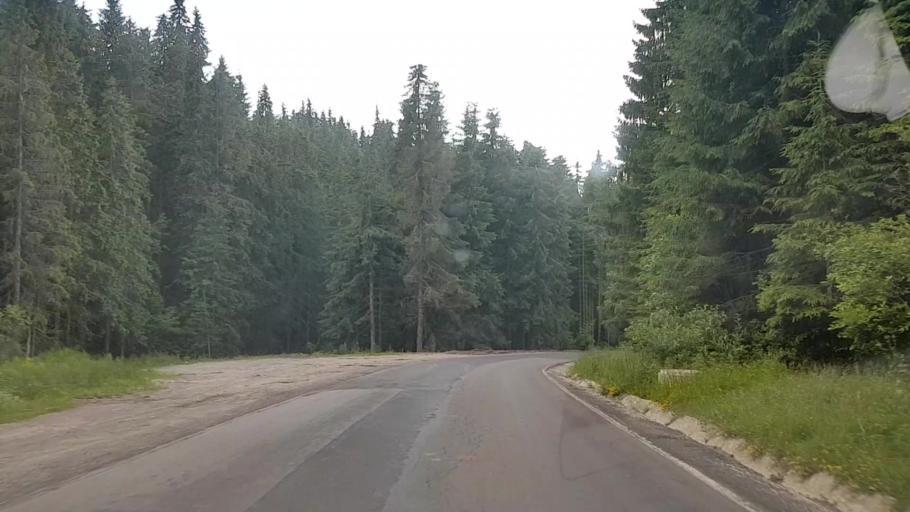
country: RO
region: Harghita
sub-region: Comuna Varsag
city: Varsag
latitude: 46.6427
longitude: 25.2843
